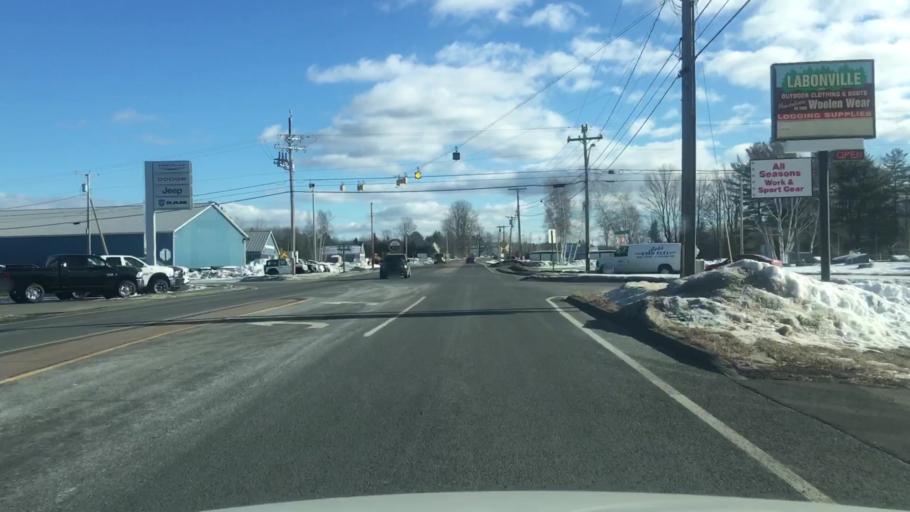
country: US
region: Maine
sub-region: Somerset County
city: Skowhegan
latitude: 44.8152
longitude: -69.7646
